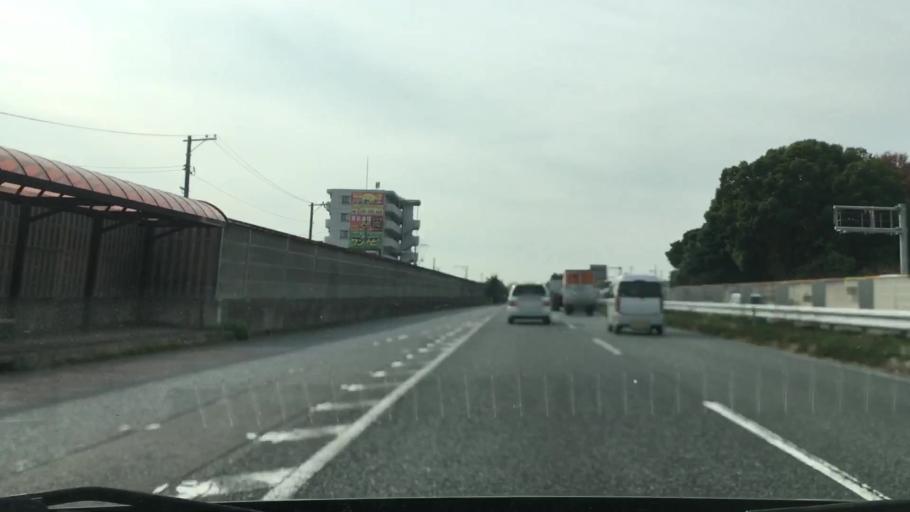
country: JP
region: Hiroshima
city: Hatsukaichi
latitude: 34.3799
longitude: 132.3485
